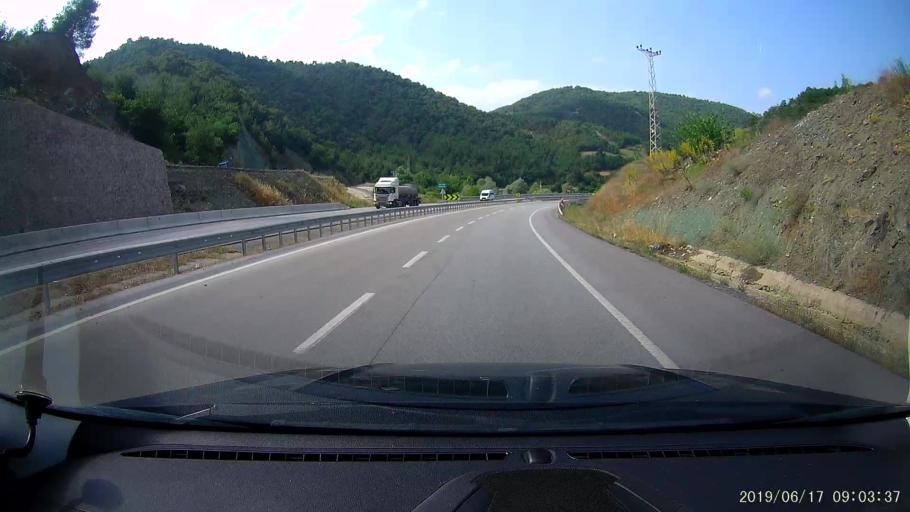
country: TR
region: Amasya
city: Tasova
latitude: 40.7528
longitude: 36.3022
